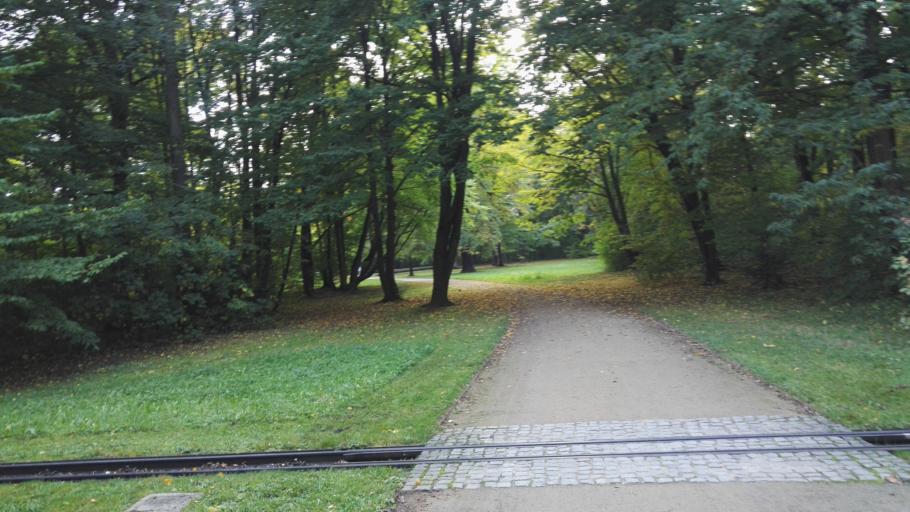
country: DE
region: Saxony
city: Dresden
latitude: 51.0359
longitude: 13.7633
